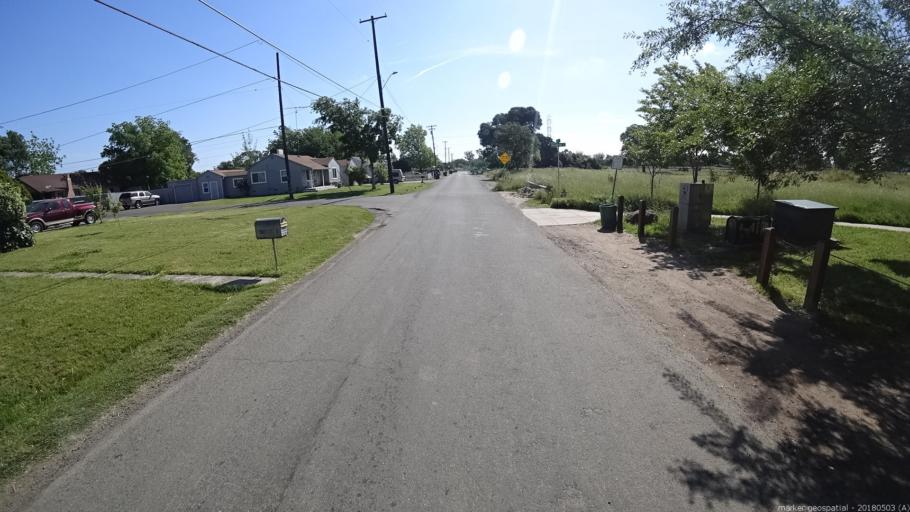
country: US
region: California
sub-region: Sacramento County
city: Arden-Arcade
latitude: 38.6255
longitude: -121.4233
